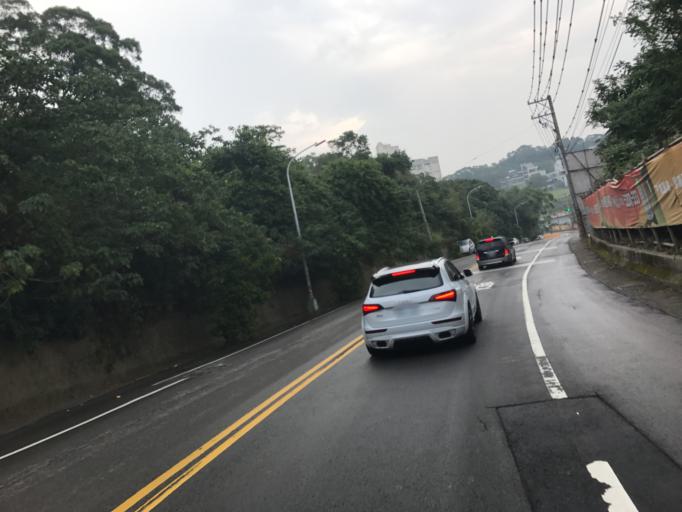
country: TW
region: Taiwan
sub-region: Hsinchu
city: Hsinchu
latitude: 24.7691
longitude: 120.9645
